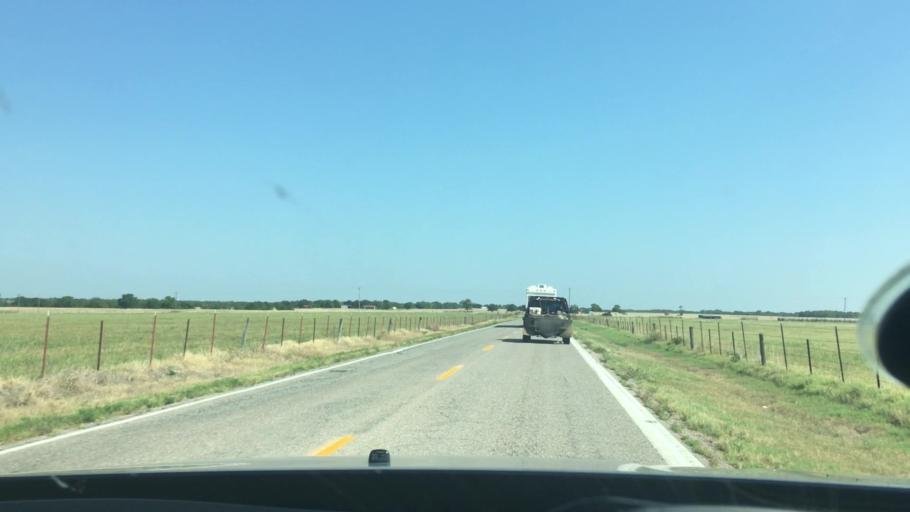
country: US
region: Oklahoma
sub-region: Johnston County
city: Tishomingo
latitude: 34.1692
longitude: -96.5095
